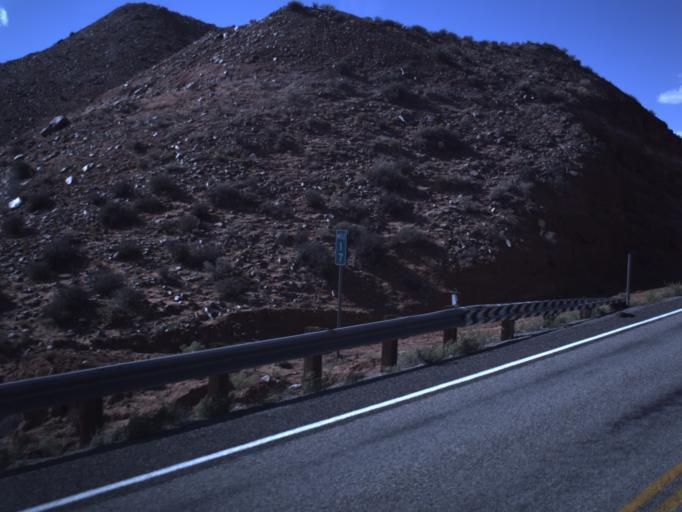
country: US
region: Utah
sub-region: Wayne County
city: Loa
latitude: 38.1421
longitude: -110.6104
